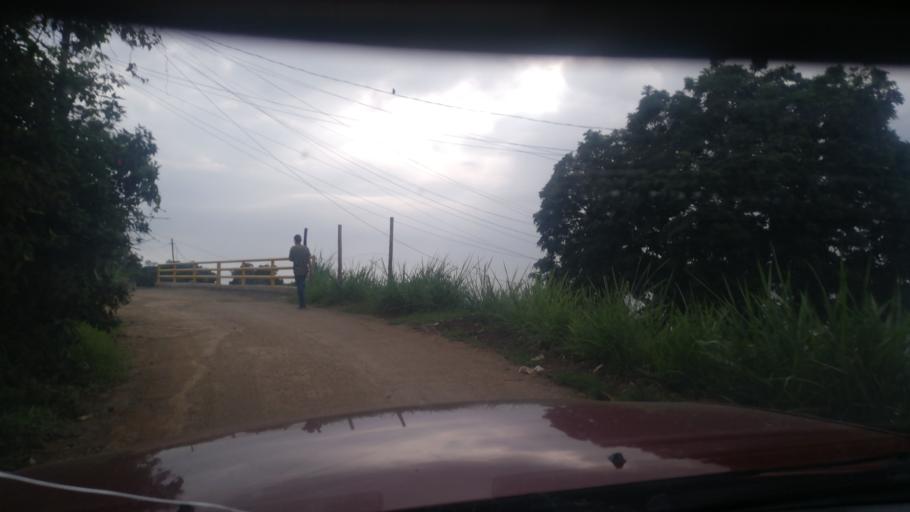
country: CO
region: Valle del Cauca
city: Cali
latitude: 3.5036
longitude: -76.5458
